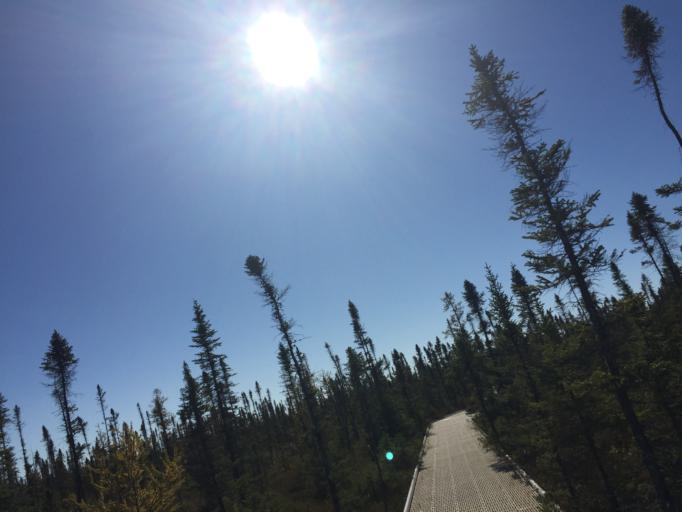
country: US
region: Minnesota
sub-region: Lake of the Woods County
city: Baudette
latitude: 48.2978
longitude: -94.5671
